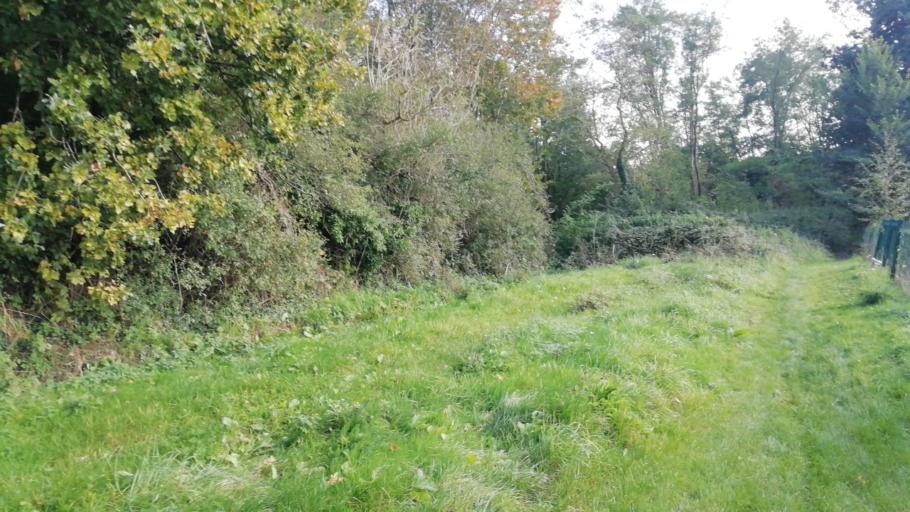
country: FR
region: Haute-Normandie
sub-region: Departement de la Seine-Maritime
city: Rolleville
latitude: 49.5961
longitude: 0.2137
